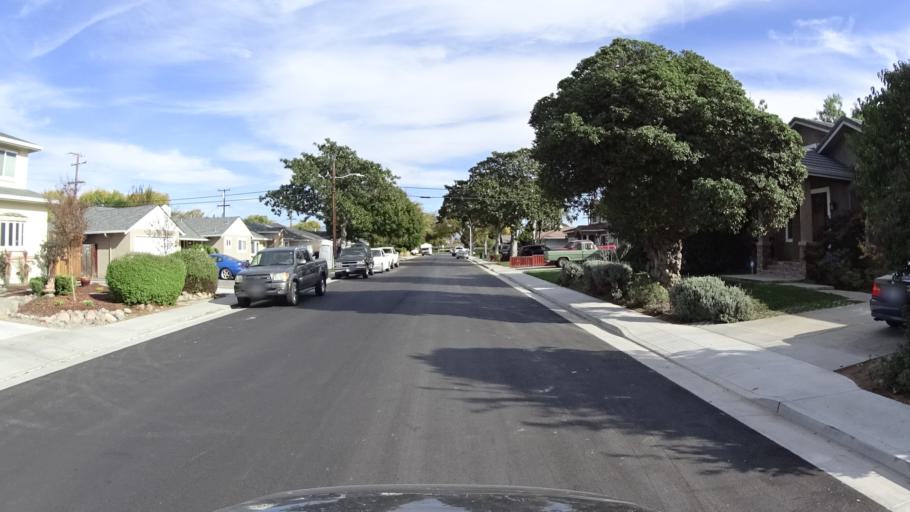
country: US
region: California
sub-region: Santa Clara County
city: Santa Clara
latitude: 37.3533
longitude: -121.9672
